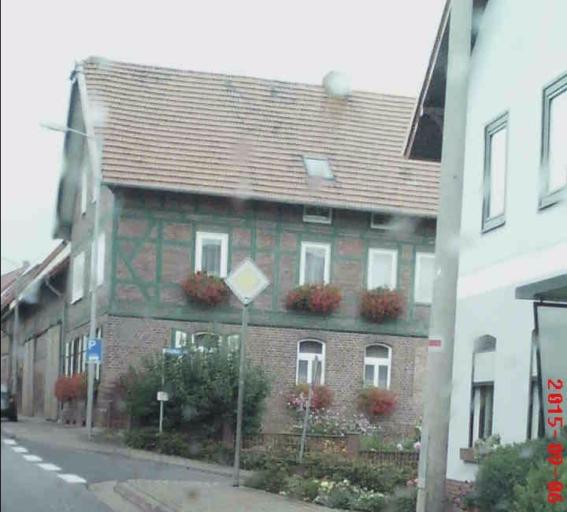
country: DE
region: Thuringia
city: Weissenborn-Luderode
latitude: 51.5299
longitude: 10.4262
